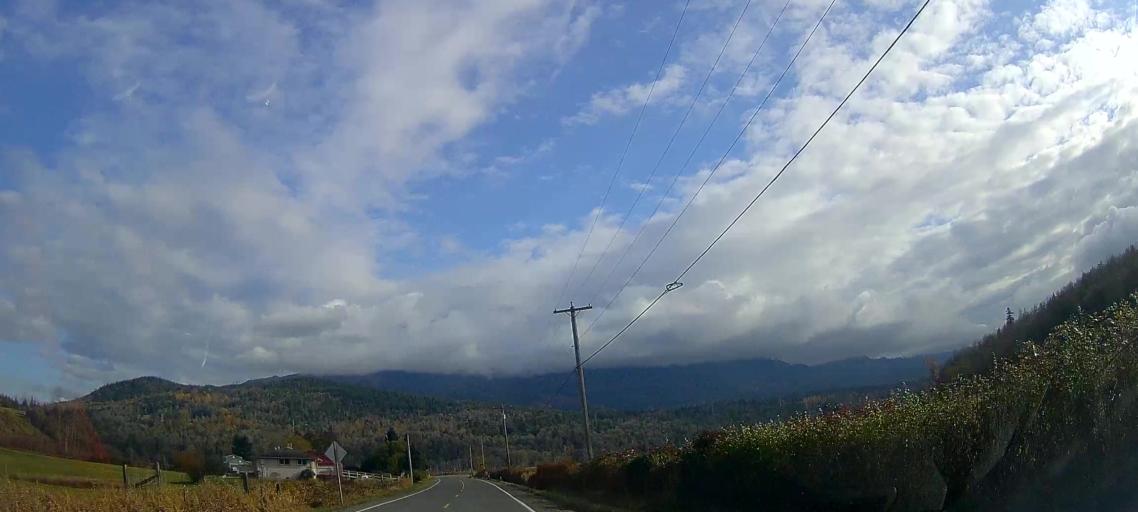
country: US
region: Washington
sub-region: Skagit County
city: Clear Lake
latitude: 48.4522
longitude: -122.2288
